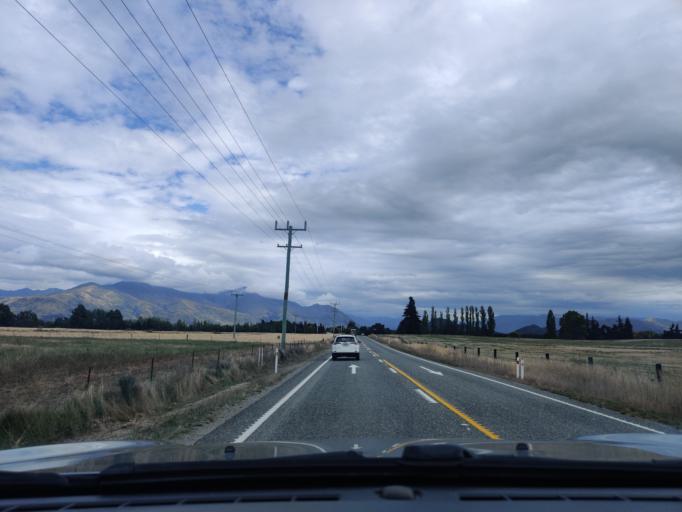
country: NZ
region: Otago
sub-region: Queenstown-Lakes District
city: Wanaka
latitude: -44.7191
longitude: 169.2226
